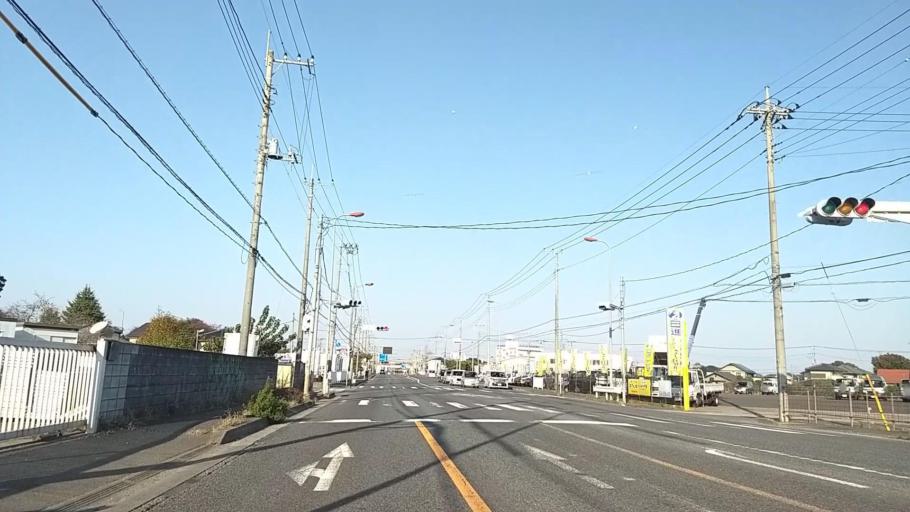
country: JP
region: Tokyo
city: Fussa
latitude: 35.7948
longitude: 139.3649
